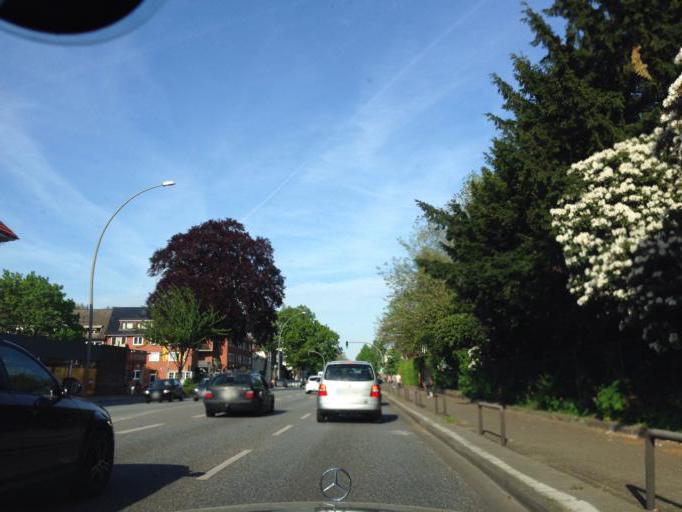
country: DE
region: Hamburg
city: Wandsbek
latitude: 53.5786
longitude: 10.0947
